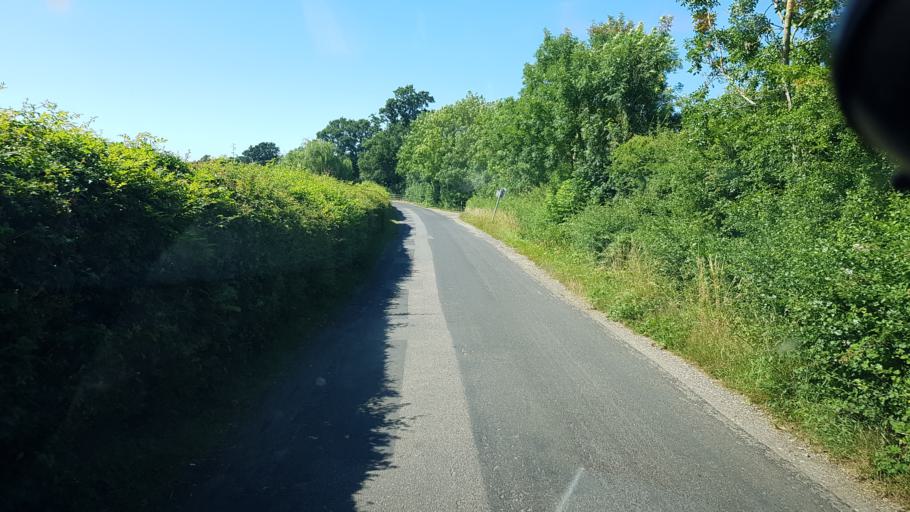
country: GB
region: England
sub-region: Kent
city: Edenbridge
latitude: 51.1948
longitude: 0.1396
